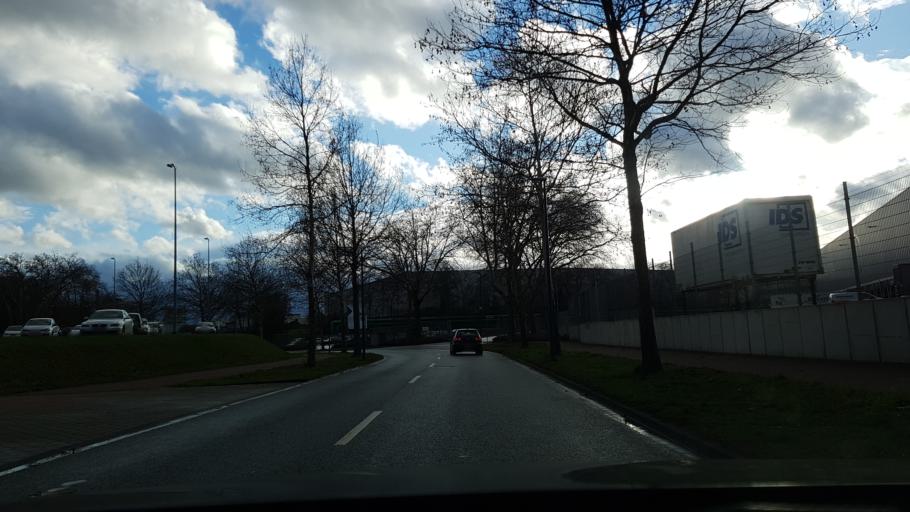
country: DE
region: North Rhine-Westphalia
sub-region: Regierungsbezirk Dusseldorf
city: Hochfeld
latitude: 51.3941
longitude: 6.7253
